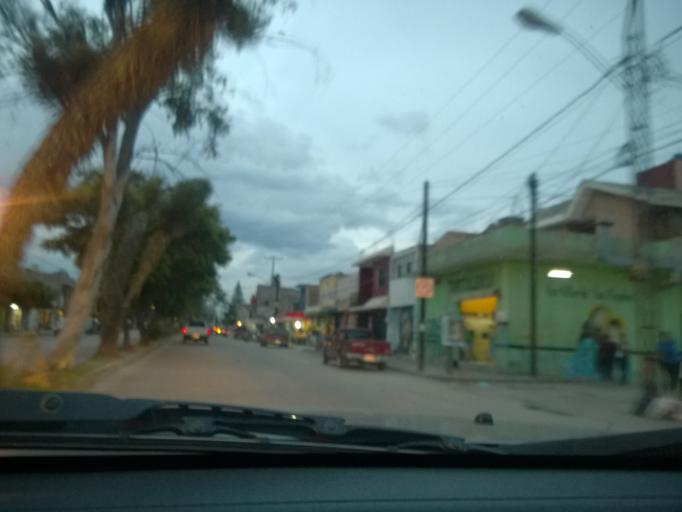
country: MX
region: Guanajuato
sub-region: Leon
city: Medina
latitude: 21.1310
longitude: -101.6426
